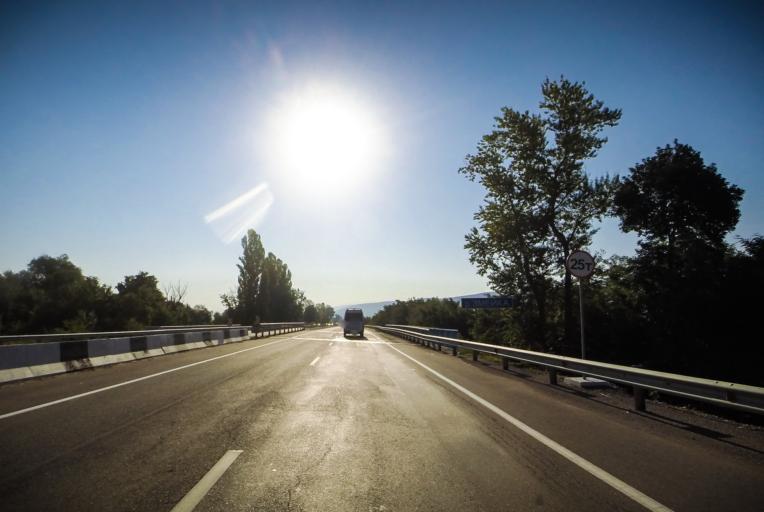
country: RU
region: North Ossetia
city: Zmeyskaya
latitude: 43.3230
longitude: 44.1241
